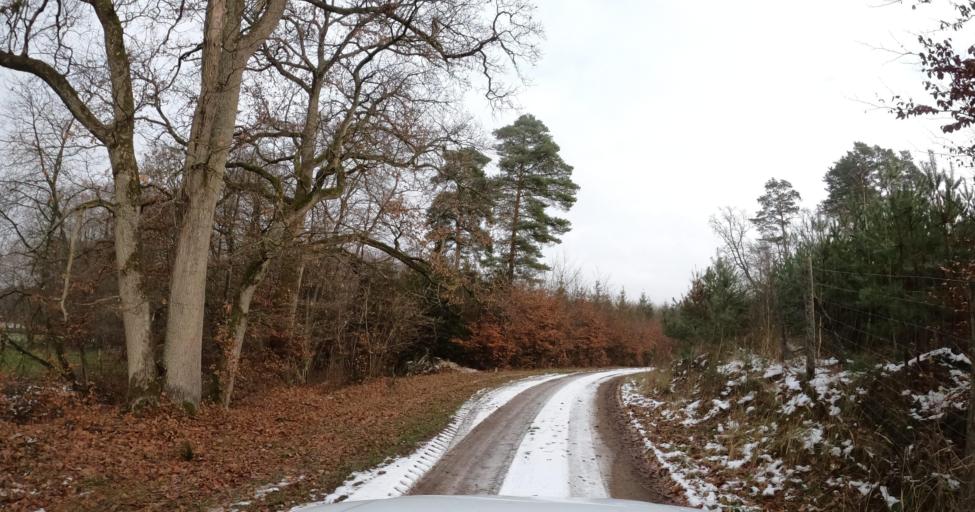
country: PL
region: West Pomeranian Voivodeship
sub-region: Powiat swidwinski
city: Rabino
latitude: 53.9120
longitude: 15.8739
